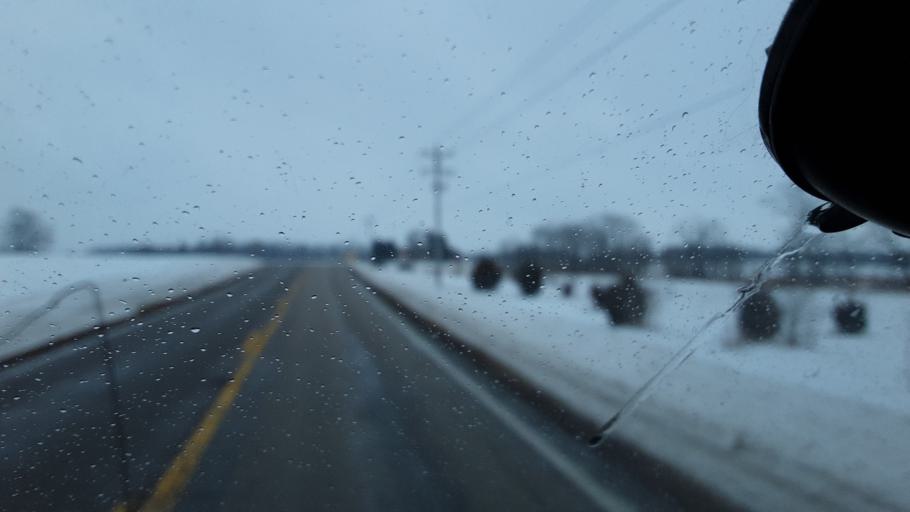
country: US
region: Ohio
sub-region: Union County
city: Marysville
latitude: 40.1849
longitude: -83.3811
